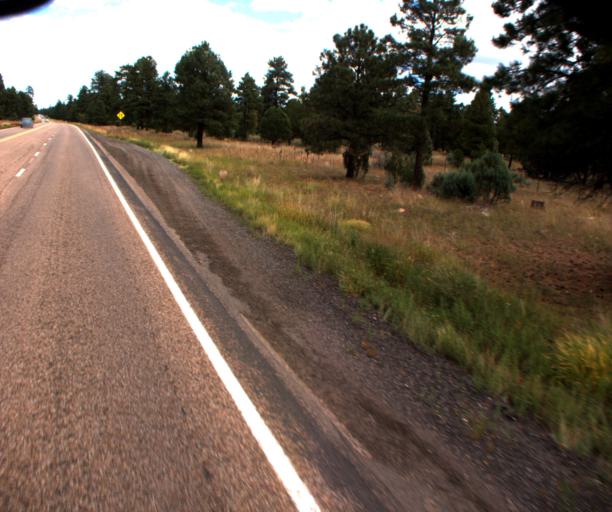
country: US
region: Arizona
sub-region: Navajo County
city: Heber-Overgaard
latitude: 34.4113
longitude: -110.6619
